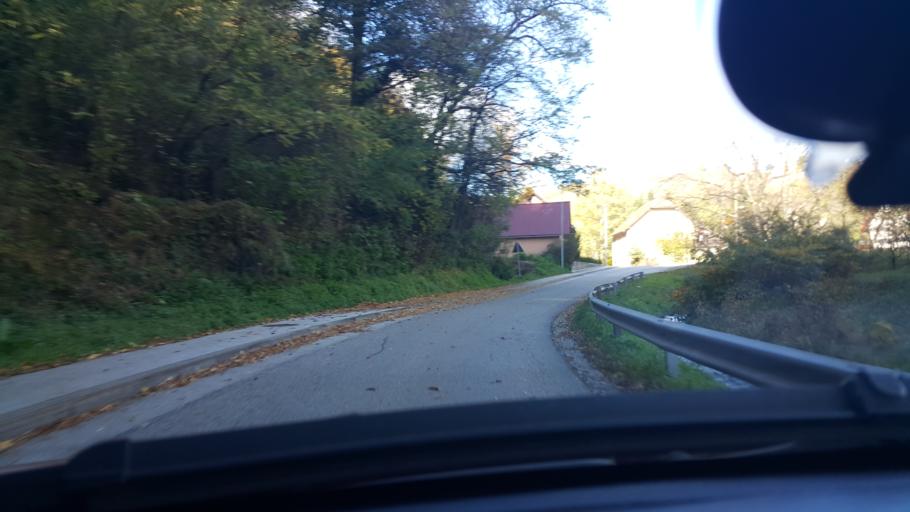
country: SI
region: Race-Fram
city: Fram
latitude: 46.4535
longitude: 15.6333
